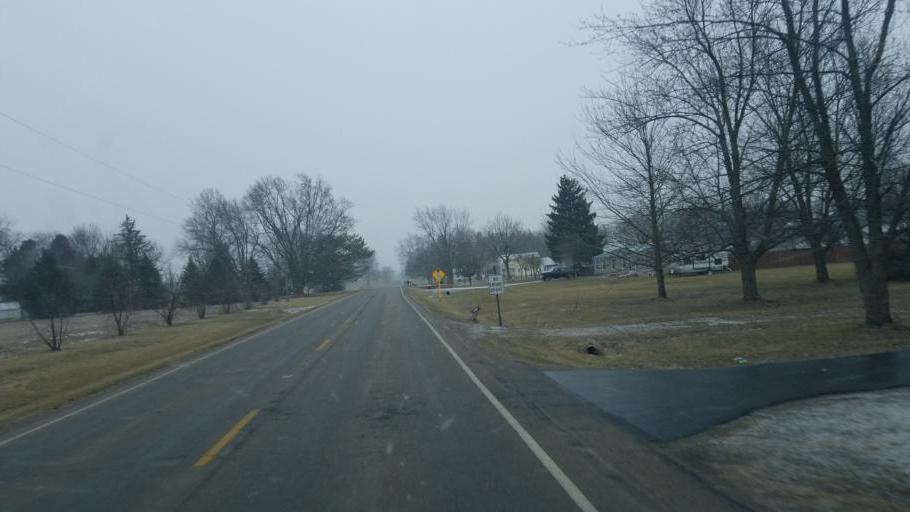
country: US
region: Ohio
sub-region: Defiance County
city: Hicksville
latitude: 41.3059
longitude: -84.7802
